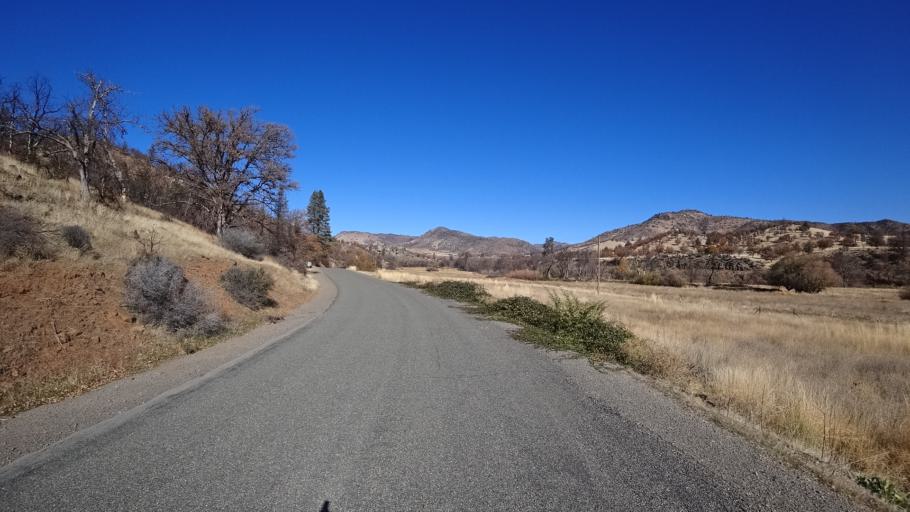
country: US
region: California
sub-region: Siskiyou County
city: Yreka
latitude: 41.9352
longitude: -122.5916
